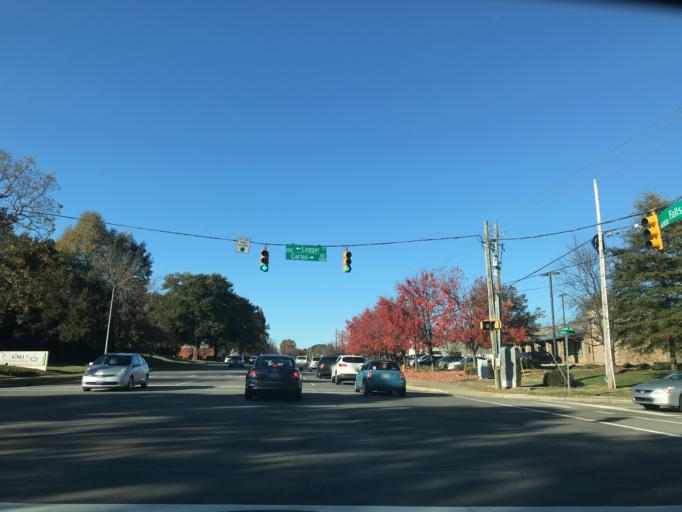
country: US
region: North Carolina
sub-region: Wake County
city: West Raleigh
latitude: 35.8641
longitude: -78.6200
